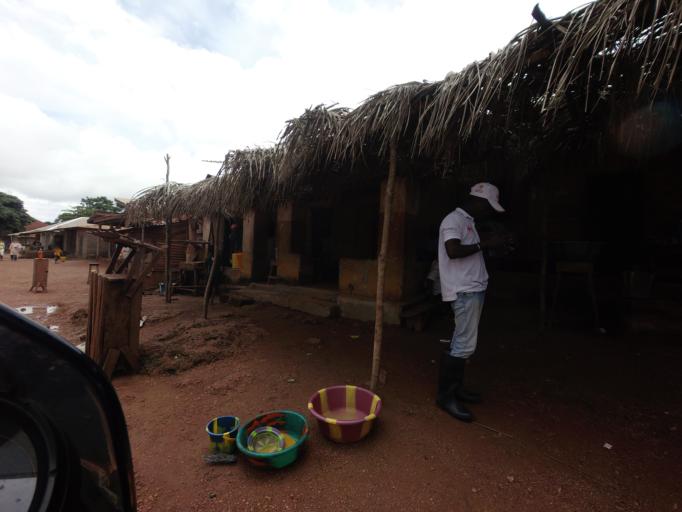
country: SL
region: Northern Province
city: Kukuna
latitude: 9.3980
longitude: -12.6648
